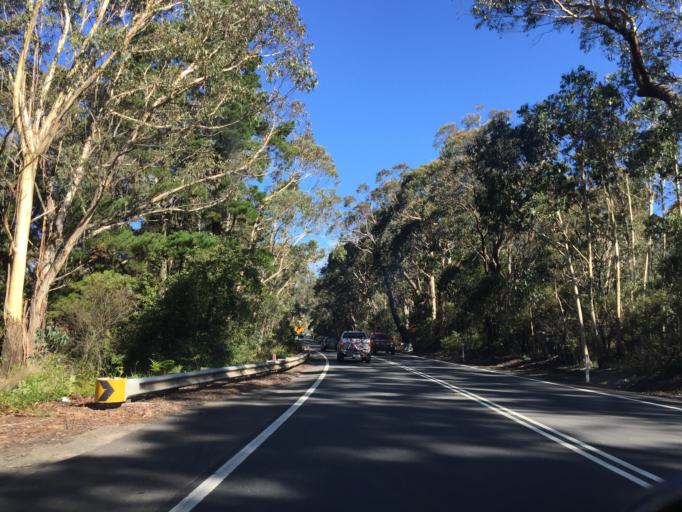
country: AU
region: New South Wales
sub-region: Blue Mountains Municipality
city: Katoomba
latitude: -33.6851
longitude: 150.2876
